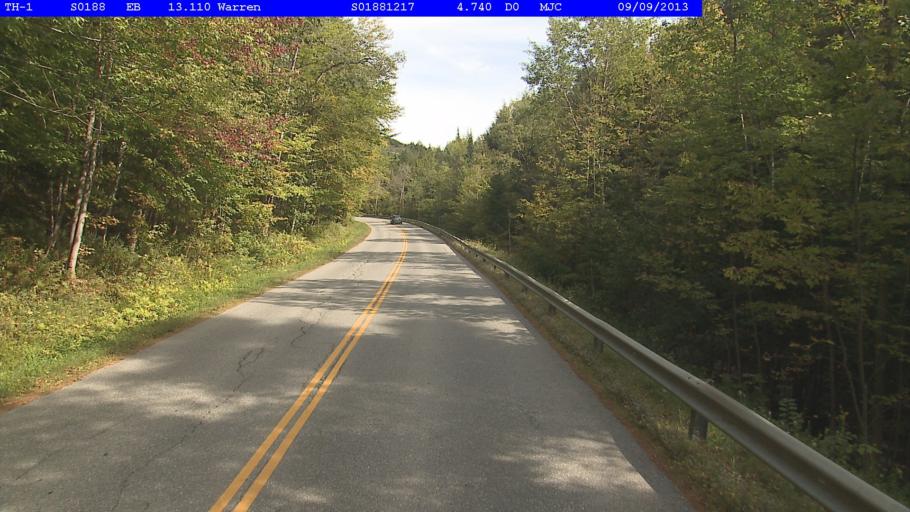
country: US
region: Vermont
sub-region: Washington County
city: Northfield
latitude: 44.1117
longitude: -72.8477
